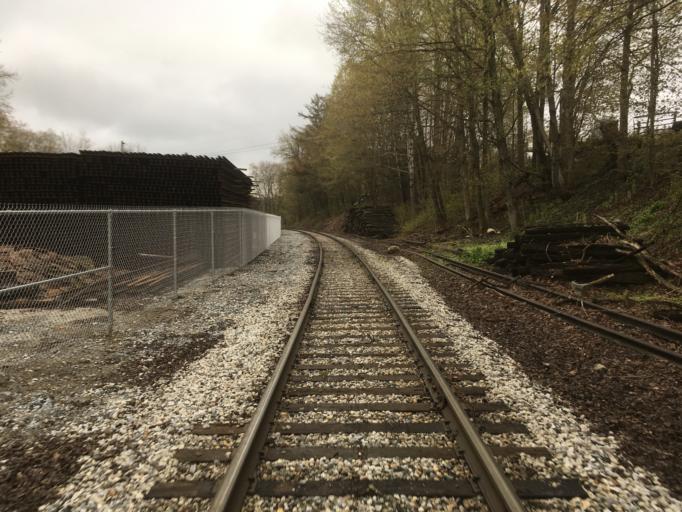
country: US
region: Vermont
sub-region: Rutland County
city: Rutland
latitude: 43.4484
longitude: -72.8768
